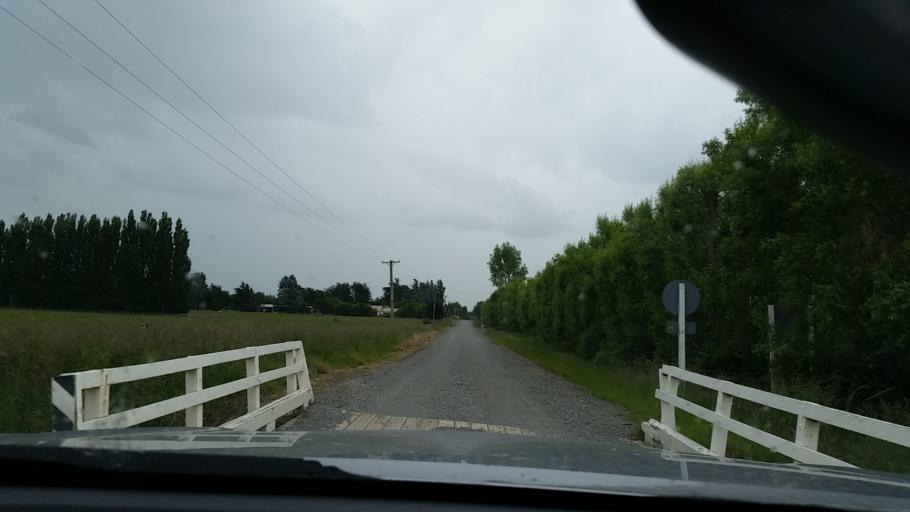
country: NZ
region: Southland
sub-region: Southland District
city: Winton
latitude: -46.0069
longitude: 168.1726
